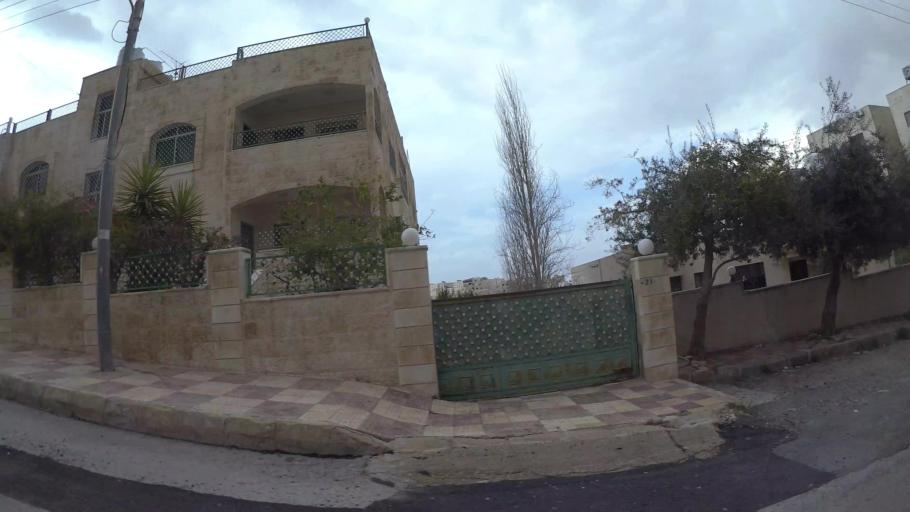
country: JO
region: Amman
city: Amman
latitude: 32.0061
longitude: 35.9437
